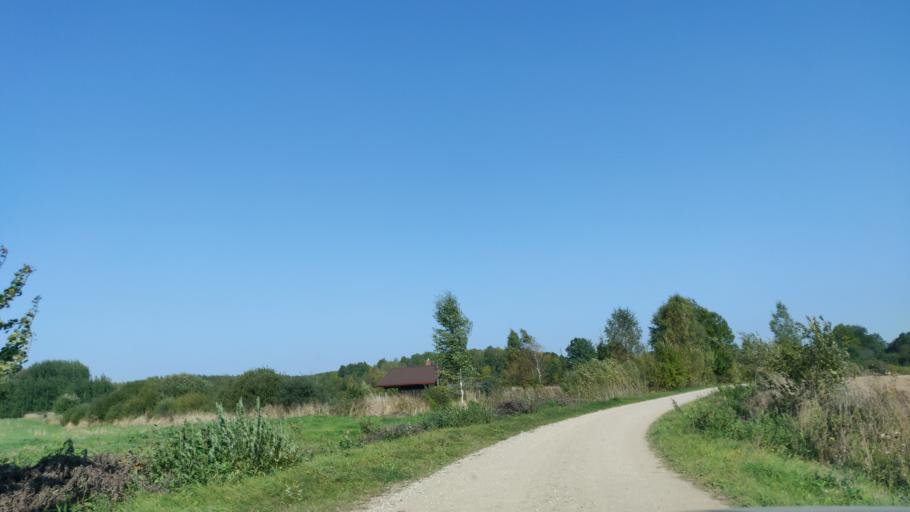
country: LT
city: Sirvintos
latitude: 54.9631
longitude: 24.7856
